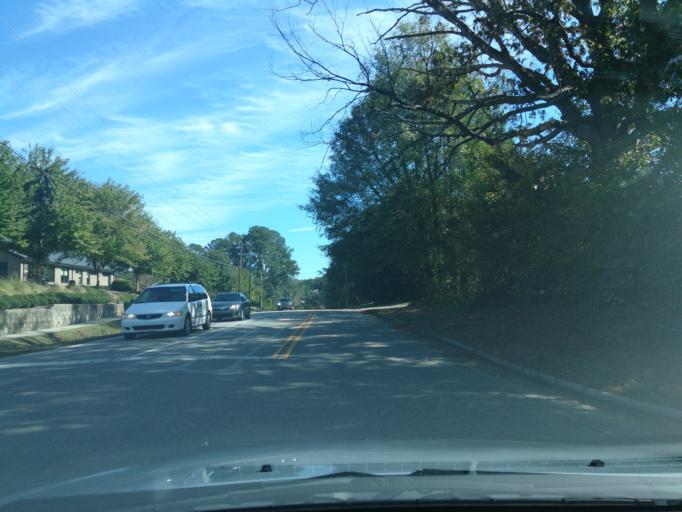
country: US
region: North Carolina
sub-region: Durham County
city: Durham
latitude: 35.9755
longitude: -78.9699
